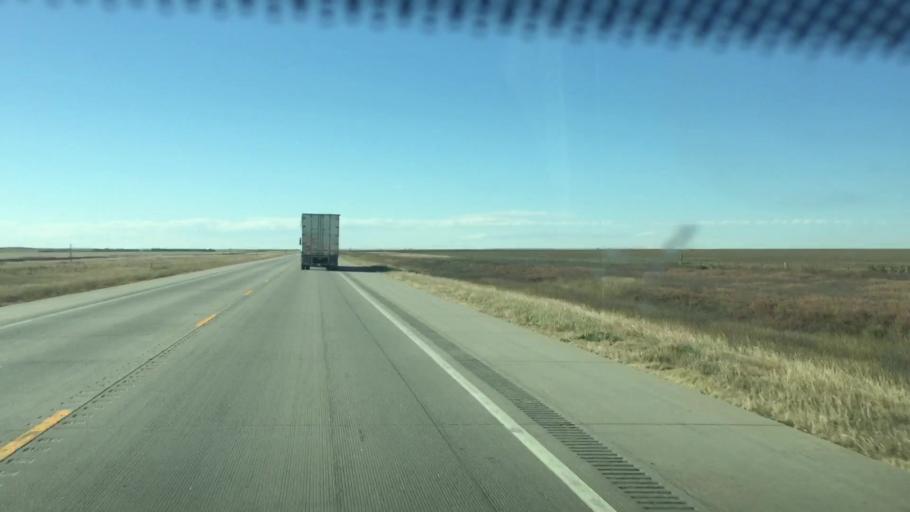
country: US
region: Colorado
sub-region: Kiowa County
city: Eads
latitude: 38.7918
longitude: -102.9370
